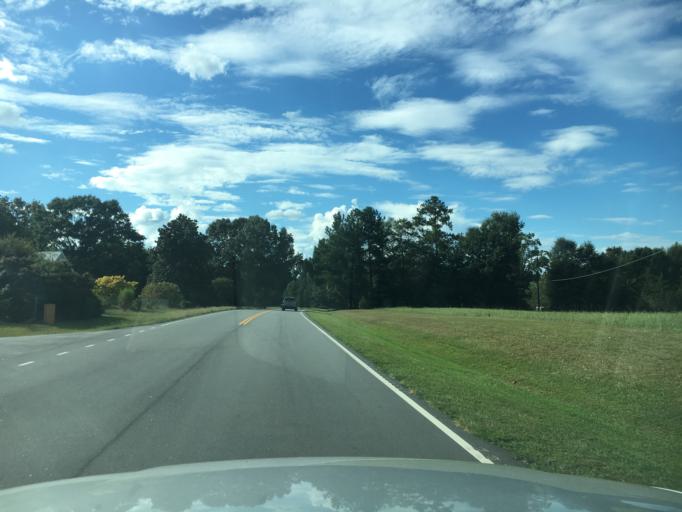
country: US
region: South Carolina
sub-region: Greenwood County
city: Ware Shoals
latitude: 34.5099
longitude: -82.1827
